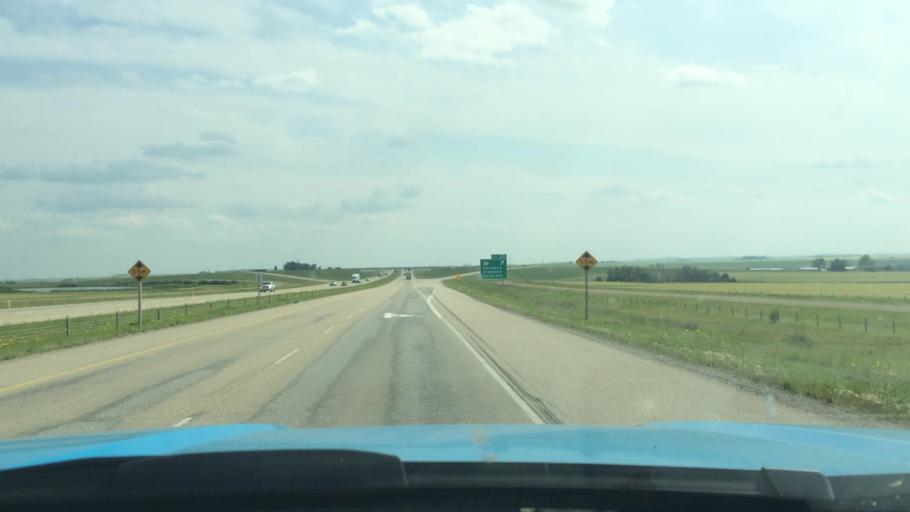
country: CA
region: Alberta
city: Carstairs
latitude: 51.5697
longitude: -114.0252
